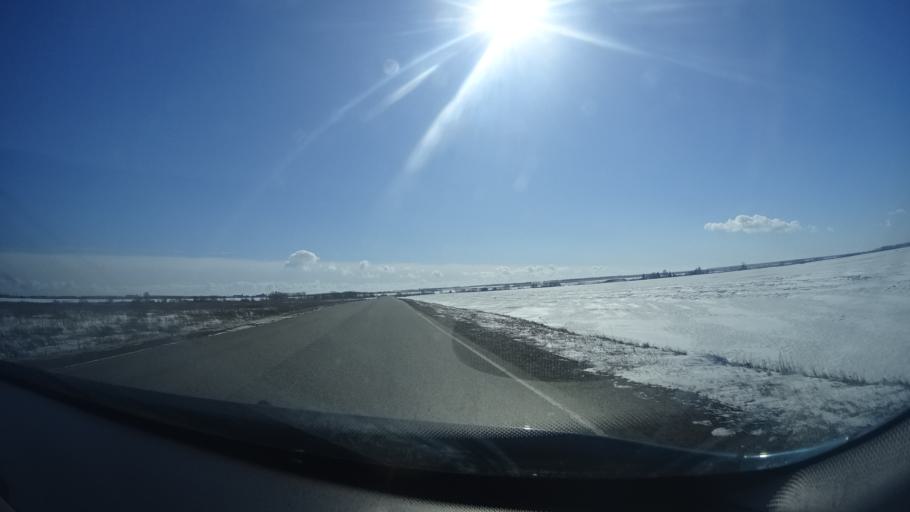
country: RU
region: Bashkortostan
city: Avdon
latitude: 54.5920
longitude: 55.8543
